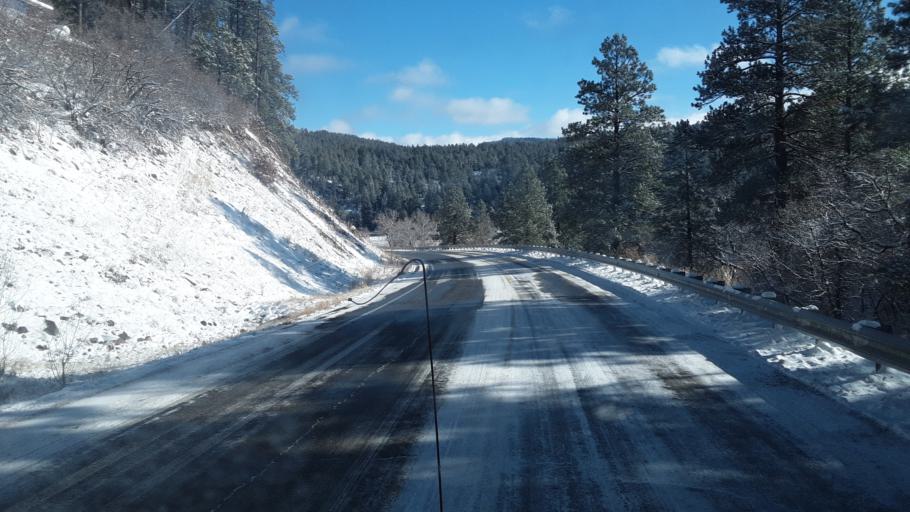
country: US
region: Colorado
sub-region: La Plata County
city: Durango
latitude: 37.3317
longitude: -107.7294
